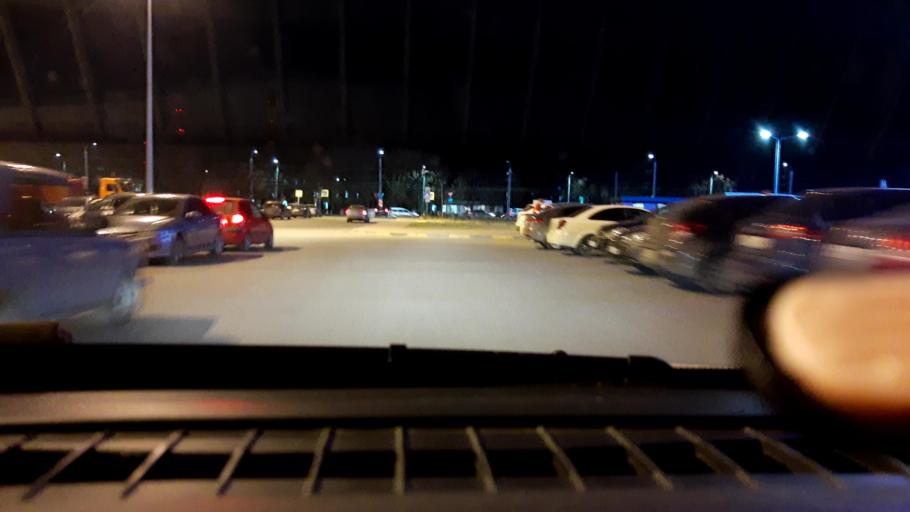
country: RU
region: Nizjnij Novgorod
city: Gorbatovka
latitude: 56.2491
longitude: 43.8781
